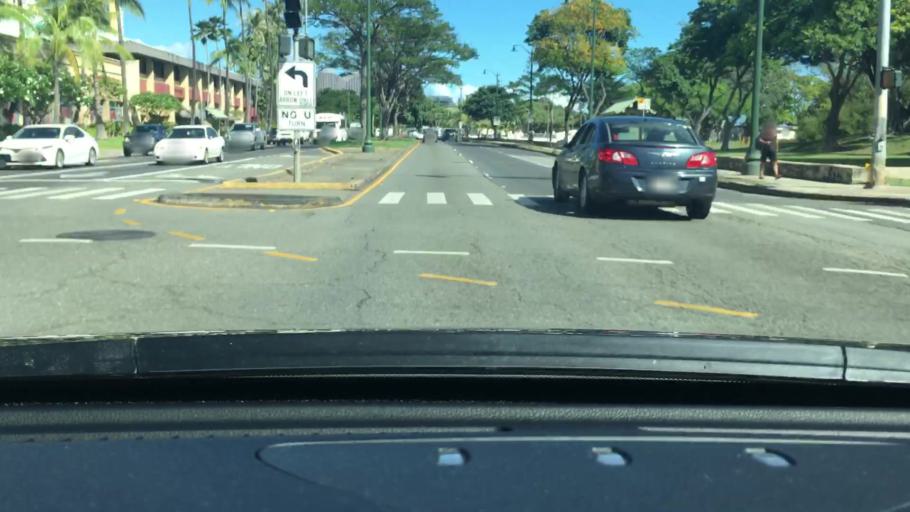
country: US
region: Hawaii
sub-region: Honolulu County
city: Honolulu
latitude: 21.2930
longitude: -157.8540
